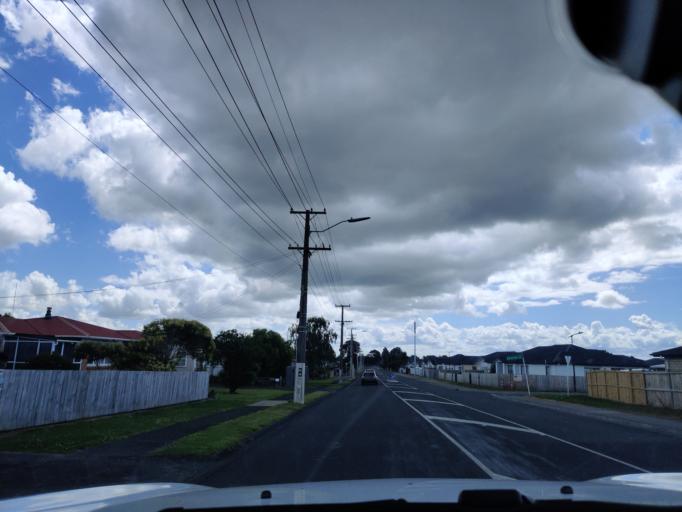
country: NZ
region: Auckland
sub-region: Auckland
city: Red Hill
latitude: -37.0535
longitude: 174.9659
